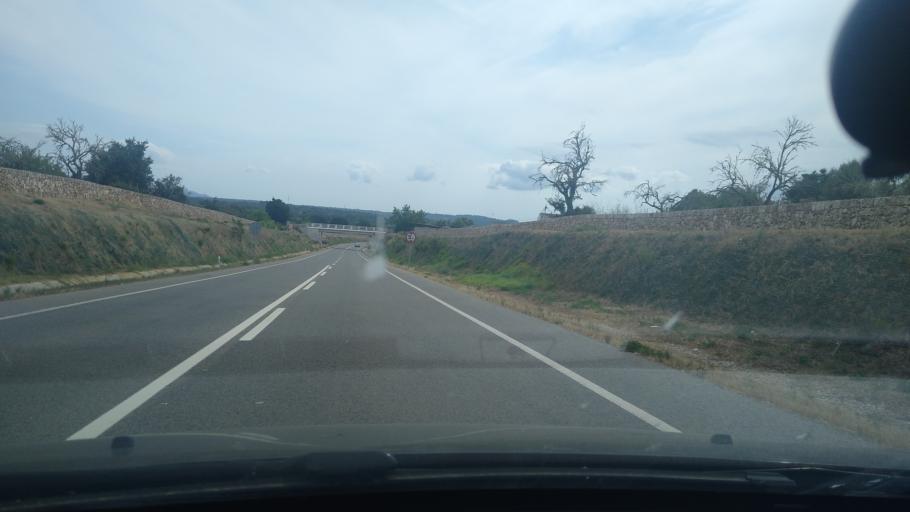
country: ES
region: Balearic Islands
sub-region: Illes Balears
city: Llubi
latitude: 39.6990
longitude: 3.0140
